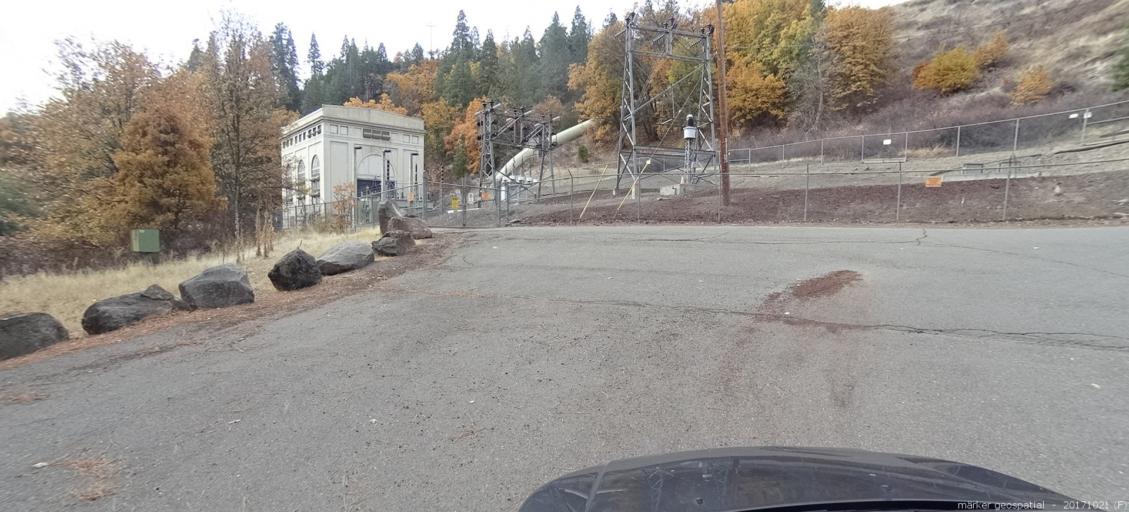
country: US
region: California
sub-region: Shasta County
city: Burney
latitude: 40.9613
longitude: -121.5483
